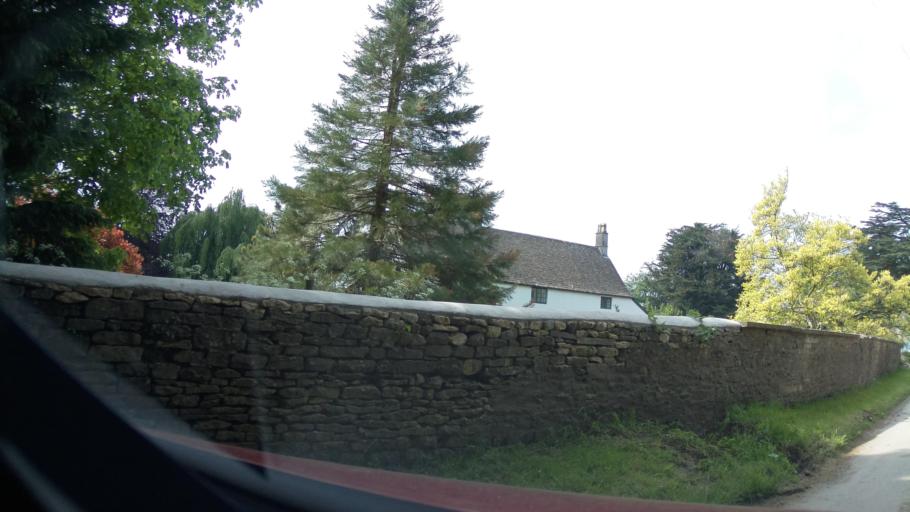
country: GB
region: England
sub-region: South Gloucestershire
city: Horton
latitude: 51.5455
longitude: -2.3514
